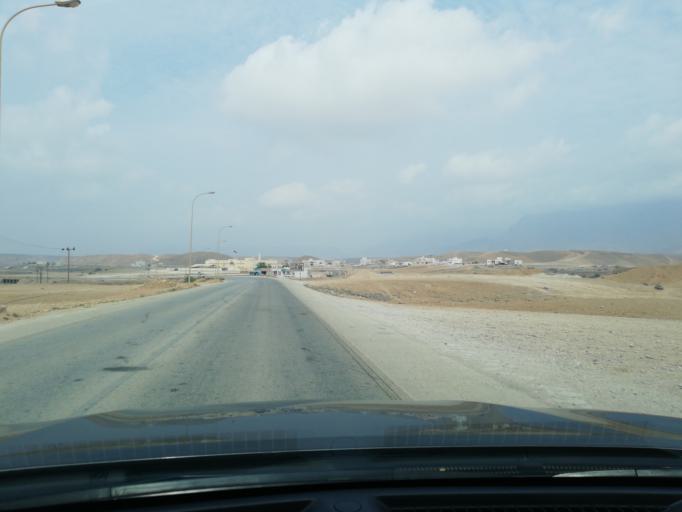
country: OM
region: Zufar
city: Salalah
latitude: 16.9608
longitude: 53.8725
